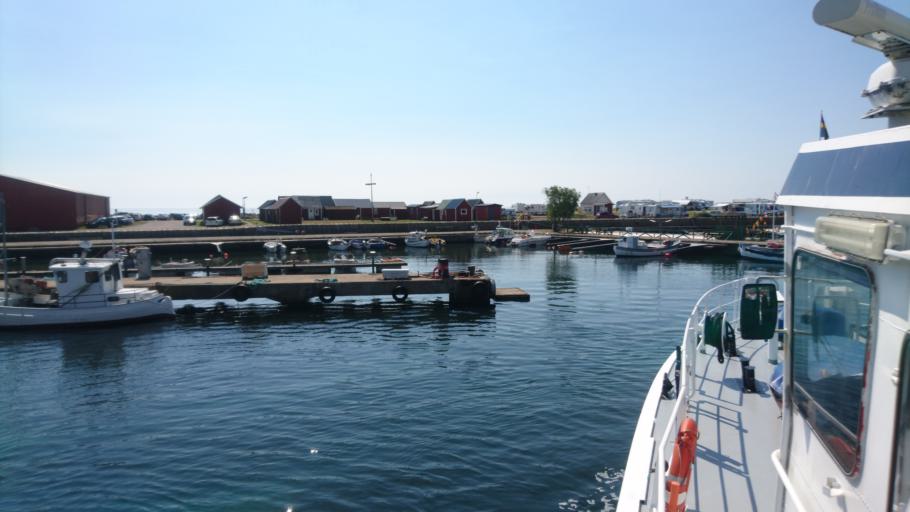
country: SE
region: Blekinge
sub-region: Solvesborgs Kommun
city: Soelvesborg
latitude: 56.0048
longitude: 14.7367
